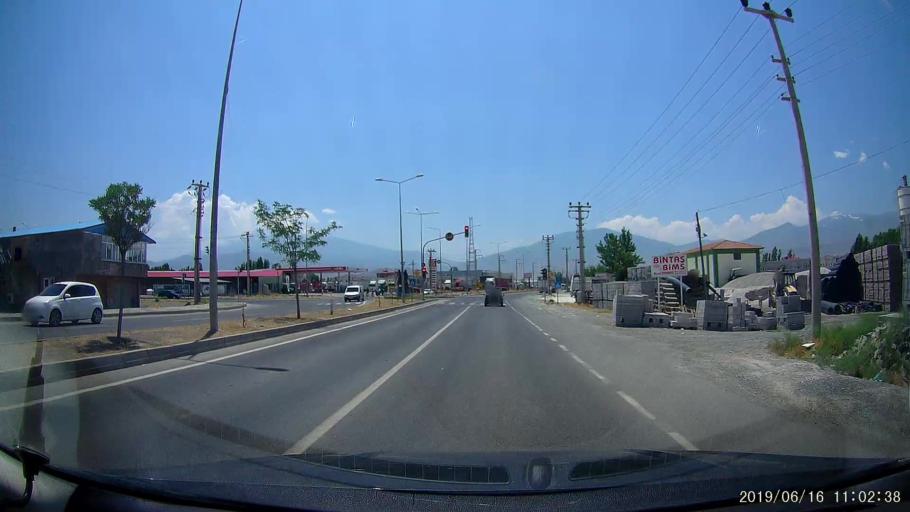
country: TR
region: Igdir
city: Igdir
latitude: 39.9098
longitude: 44.0589
